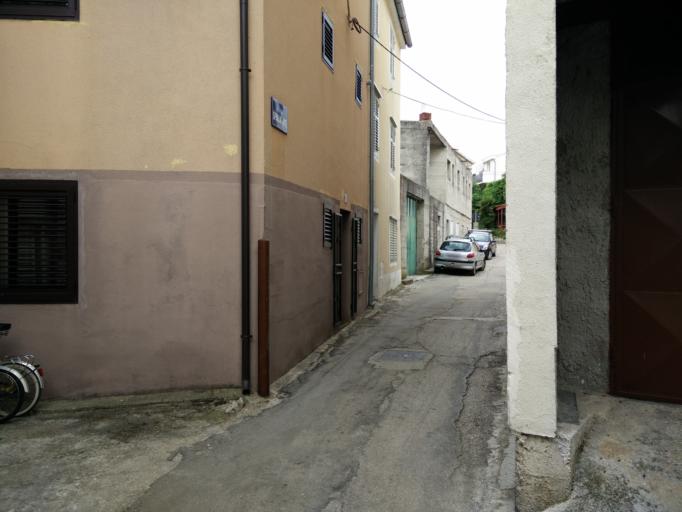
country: HR
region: Sibensko-Kniniska
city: Vodice
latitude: 43.7573
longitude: 15.7722
